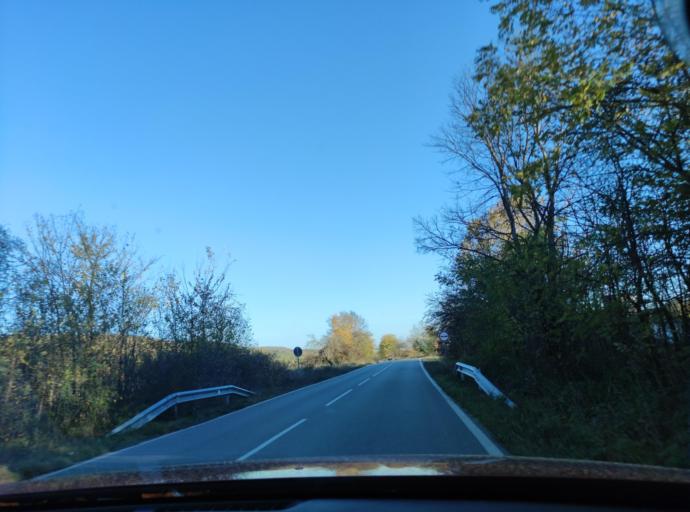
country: BG
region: Montana
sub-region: Obshtina Chiprovtsi
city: Chiprovtsi
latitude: 43.4181
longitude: 23.0262
